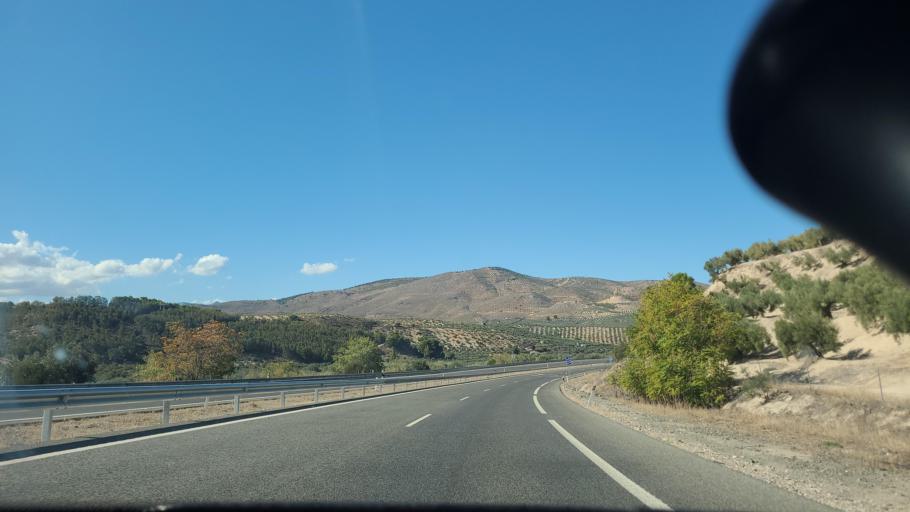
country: ES
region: Andalusia
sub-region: Provincia de Jaen
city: La Guardia de Jaen
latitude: 37.7176
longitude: -3.6730
